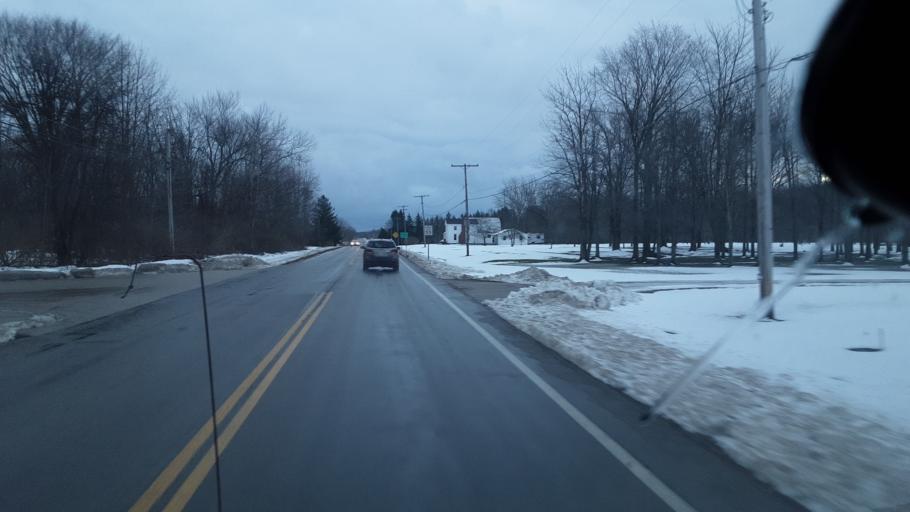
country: US
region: Ohio
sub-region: Ashtabula County
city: Jefferson
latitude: 41.7289
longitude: -80.7596
